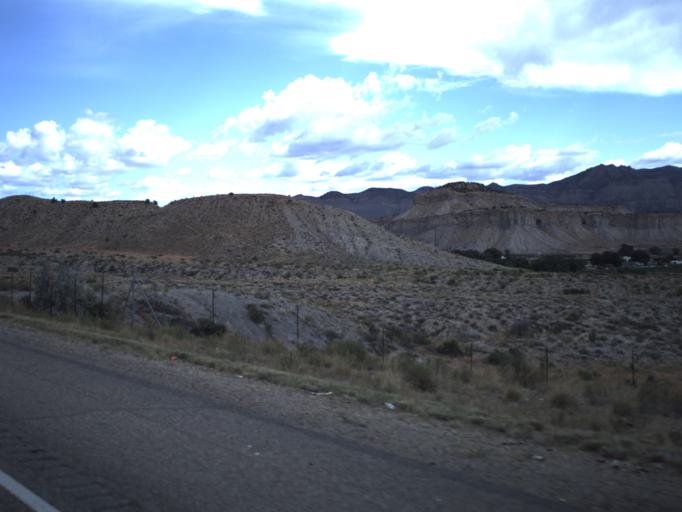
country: US
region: Utah
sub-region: Carbon County
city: Carbonville
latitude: 39.6257
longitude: -110.8595
